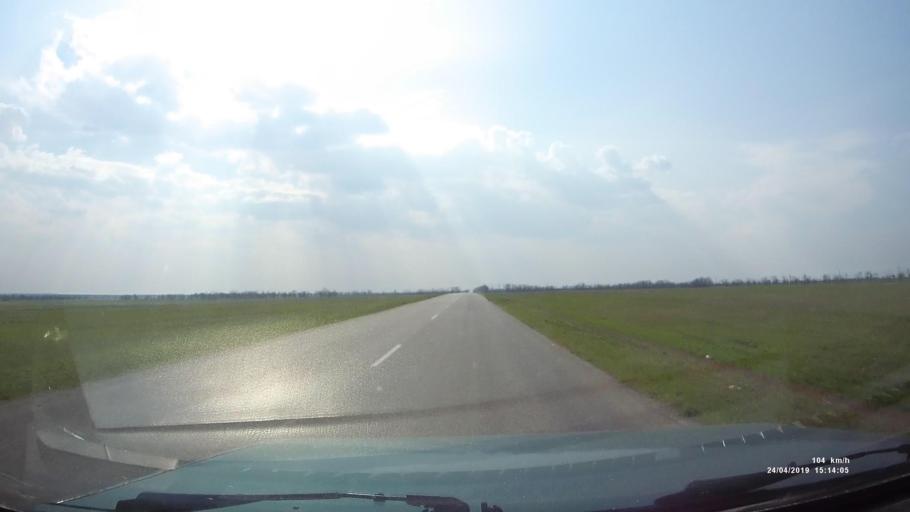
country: RU
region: Rostov
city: Remontnoye
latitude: 46.5465
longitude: 43.2654
